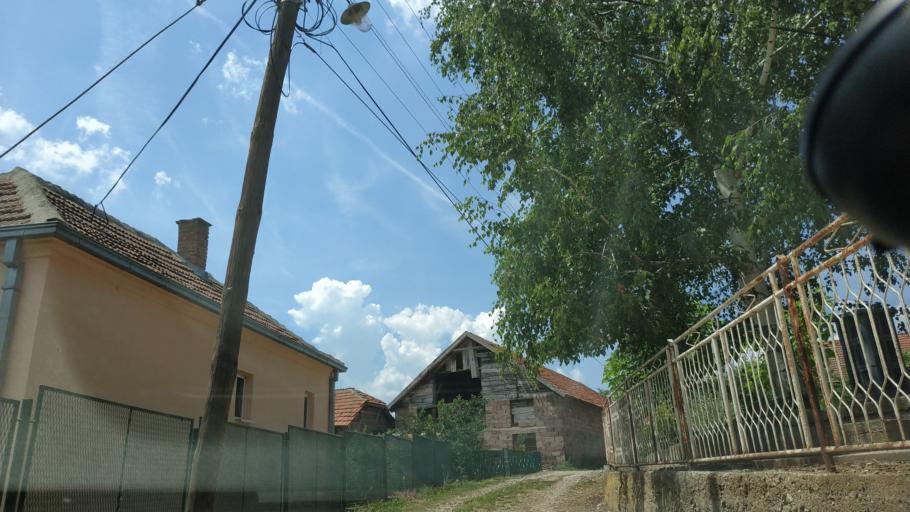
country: RS
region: Central Serbia
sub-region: Nisavski Okrug
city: Aleksinac
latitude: 43.5988
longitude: 21.6987
